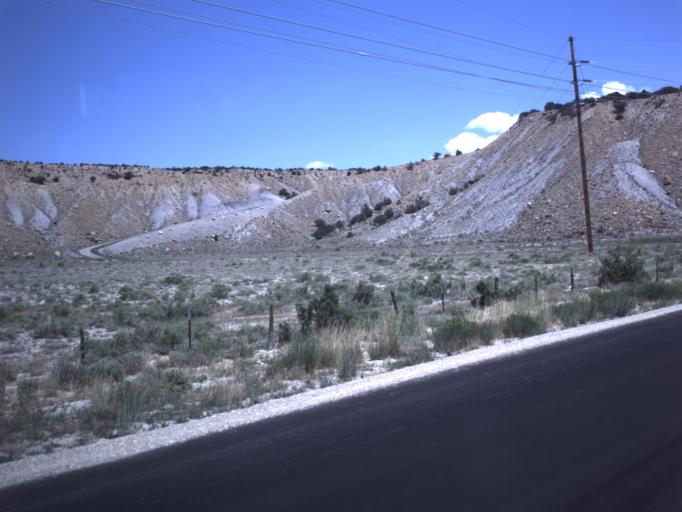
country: US
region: Utah
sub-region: Emery County
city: Orangeville
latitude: 39.2744
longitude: -111.1600
